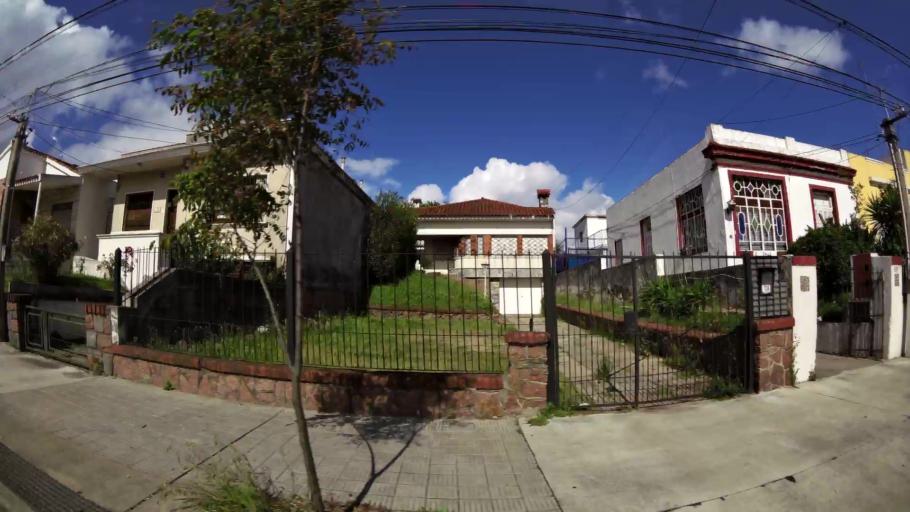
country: UY
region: Canelones
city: La Paz
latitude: -34.8231
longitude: -56.2198
